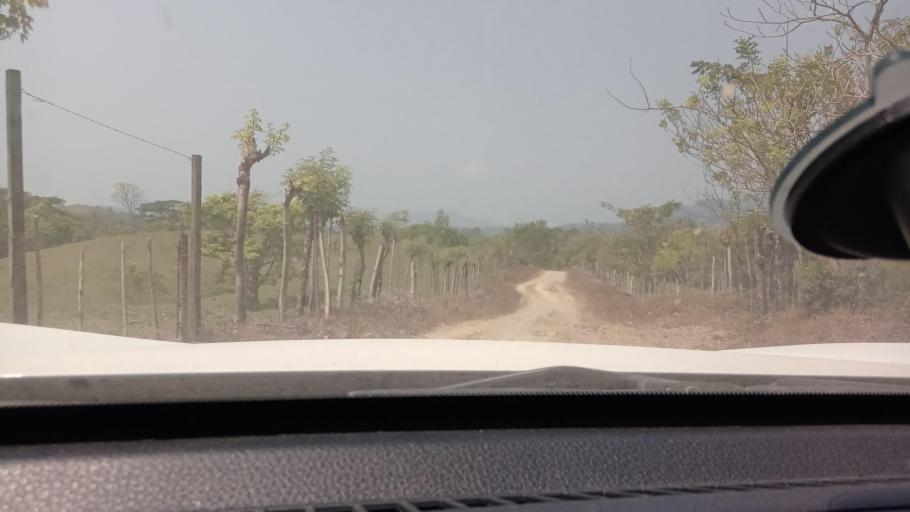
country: MX
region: Tabasco
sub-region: Huimanguillo
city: Francisco Rueda
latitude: 17.4878
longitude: -93.9330
